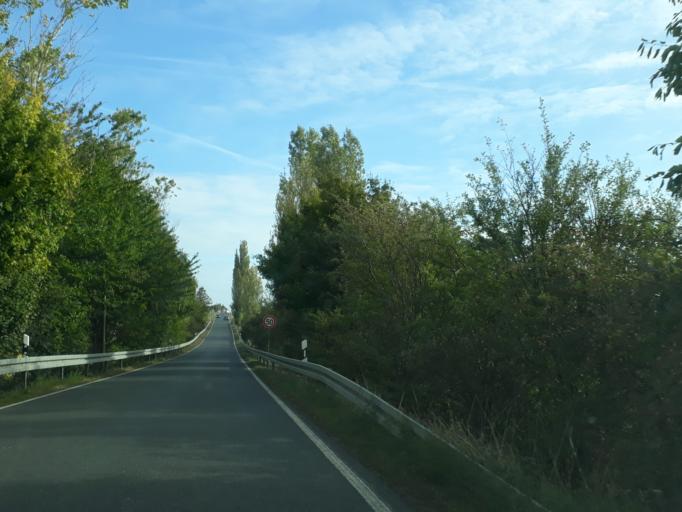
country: DE
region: Saxony
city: Wilsdruff
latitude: 51.0636
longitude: 13.5604
